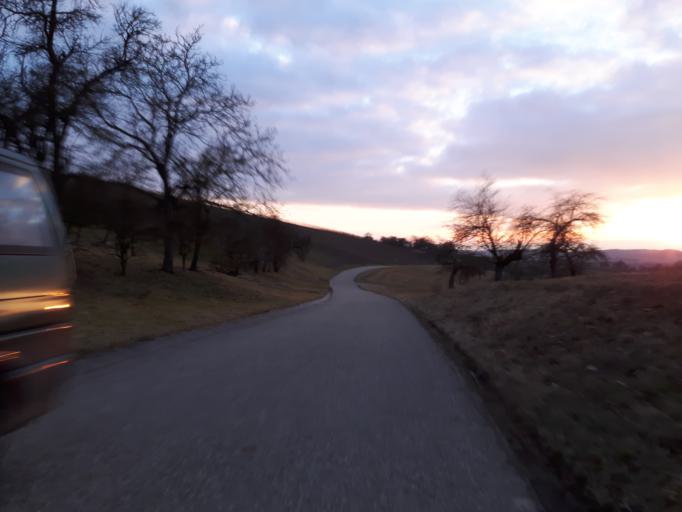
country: DE
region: Baden-Wuerttemberg
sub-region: Regierungsbezirk Stuttgart
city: Bretzfeld
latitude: 49.1811
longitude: 9.4560
